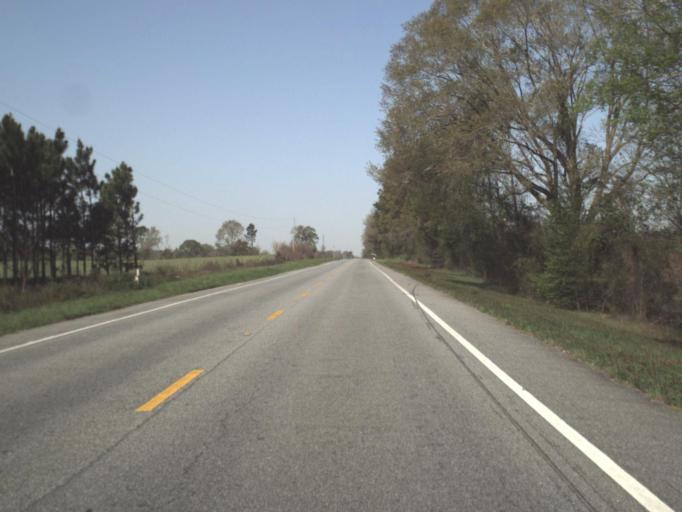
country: US
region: Florida
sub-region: Jackson County
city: Malone
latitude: 30.9760
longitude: -85.0363
